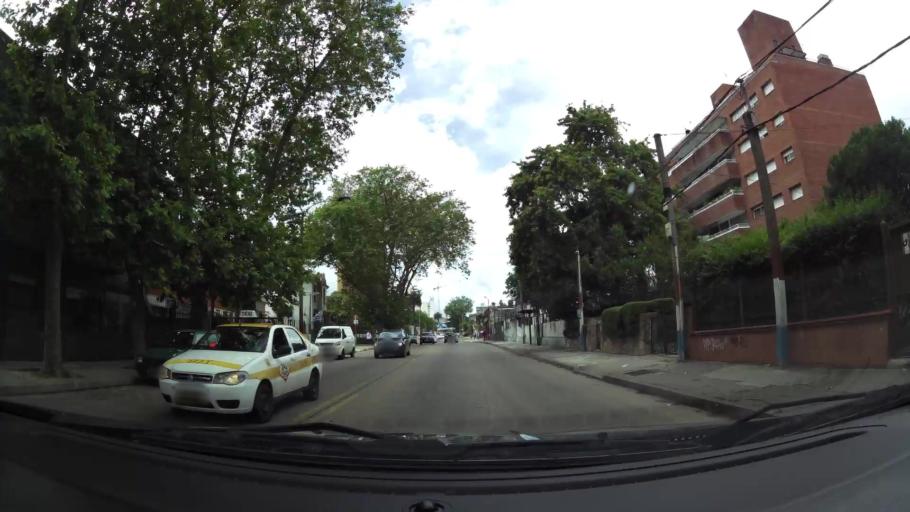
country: UY
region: Montevideo
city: Montevideo
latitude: -34.8787
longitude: -56.1557
